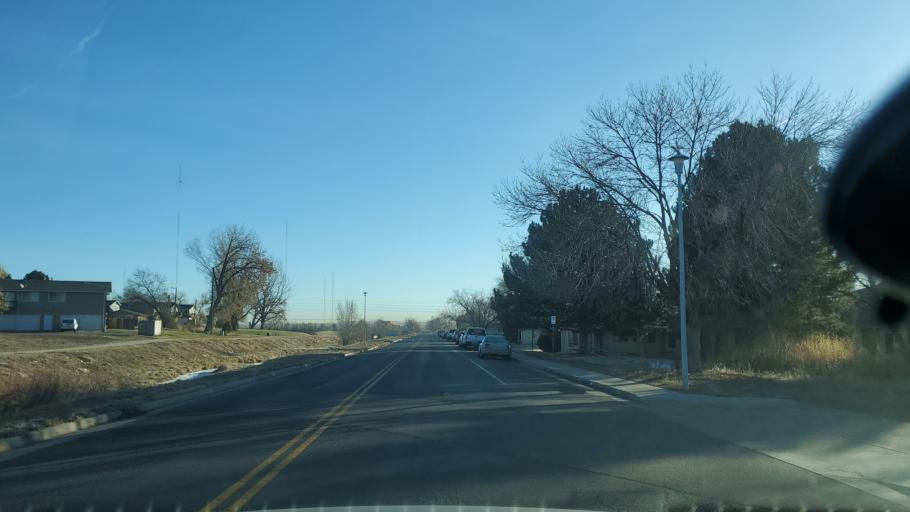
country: US
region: Colorado
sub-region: Adams County
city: Welby
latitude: 39.8418
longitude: -104.9627
